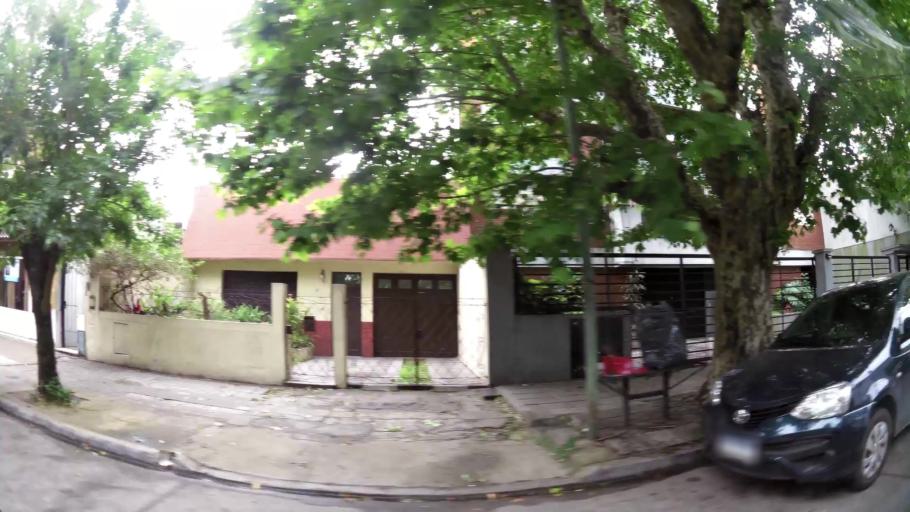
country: AR
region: Buenos Aires
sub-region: Partido de Lanus
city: Lanus
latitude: -34.7058
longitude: -58.3865
